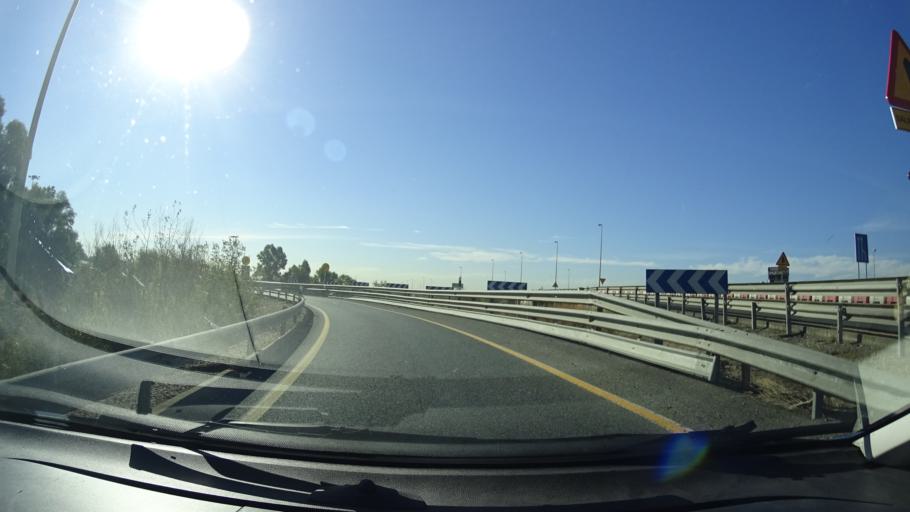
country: ES
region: Andalusia
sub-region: Provincia de Sevilla
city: Camas
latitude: 37.3888
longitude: -6.0274
